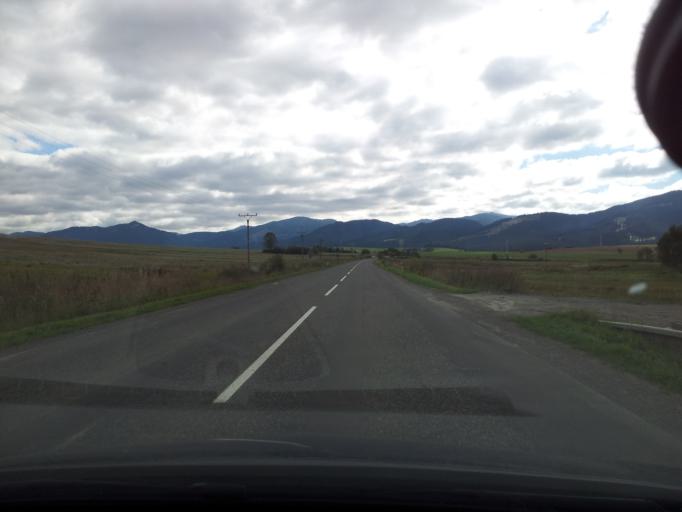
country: SK
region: Zilinsky
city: Ruzomberok
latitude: 49.0682
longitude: 19.4400
